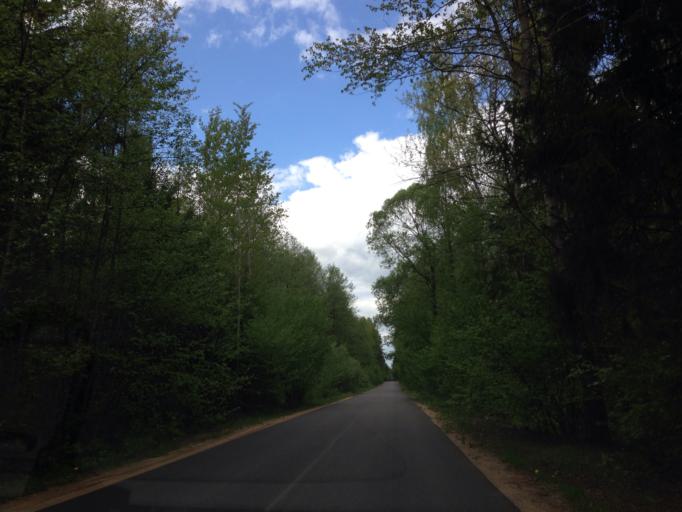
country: PL
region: Podlasie
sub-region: Powiat grajewski
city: Radzilow
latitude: 53.3309
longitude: 22.5998
